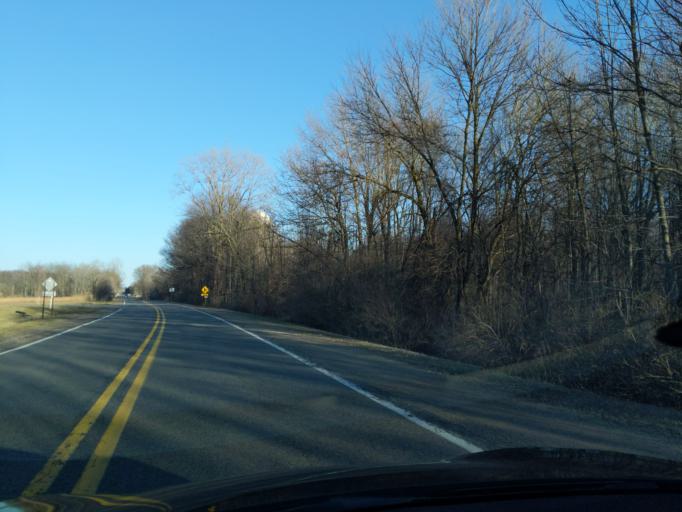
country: US
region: Michigan
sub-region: Ingham County
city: Mason
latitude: 42.5966
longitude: -84.4633
